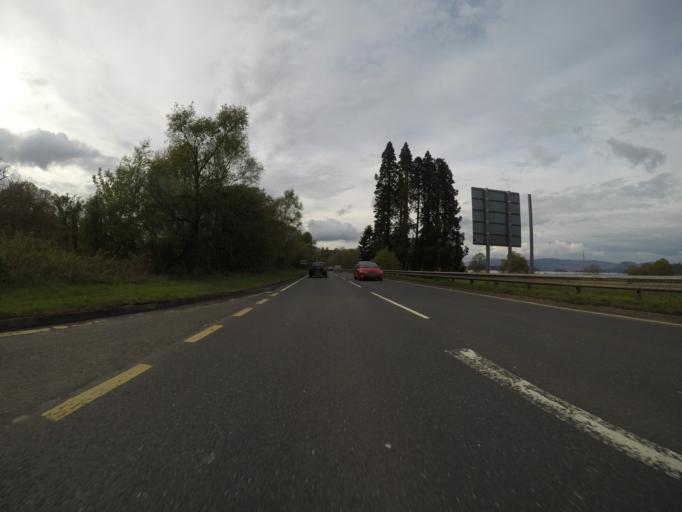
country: GB
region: Scotland
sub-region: West Dunbartonshire
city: Balloch
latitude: 56.0154
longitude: -4.6130
